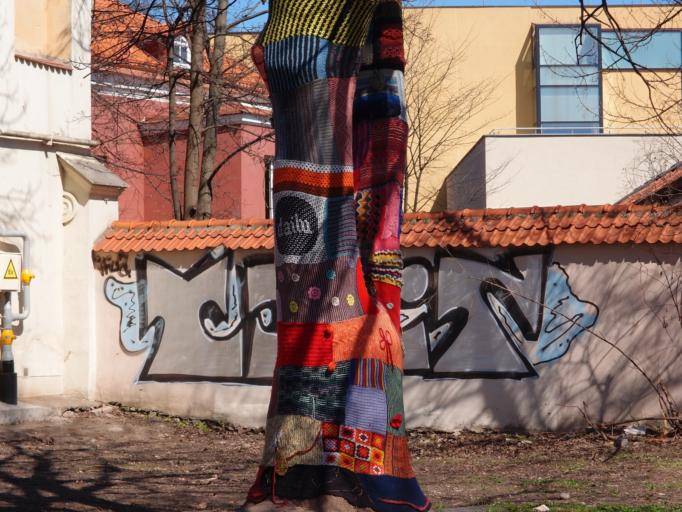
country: LT
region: Vilnius County
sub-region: Vilnius
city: Vilnius
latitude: 54.6833
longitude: 25.2924
